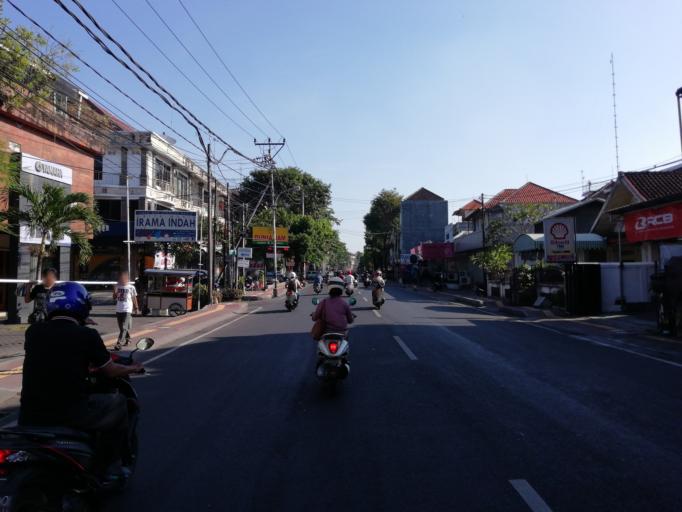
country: ID
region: Bali
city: Denpasar
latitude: -8.6638
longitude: 115.2153
